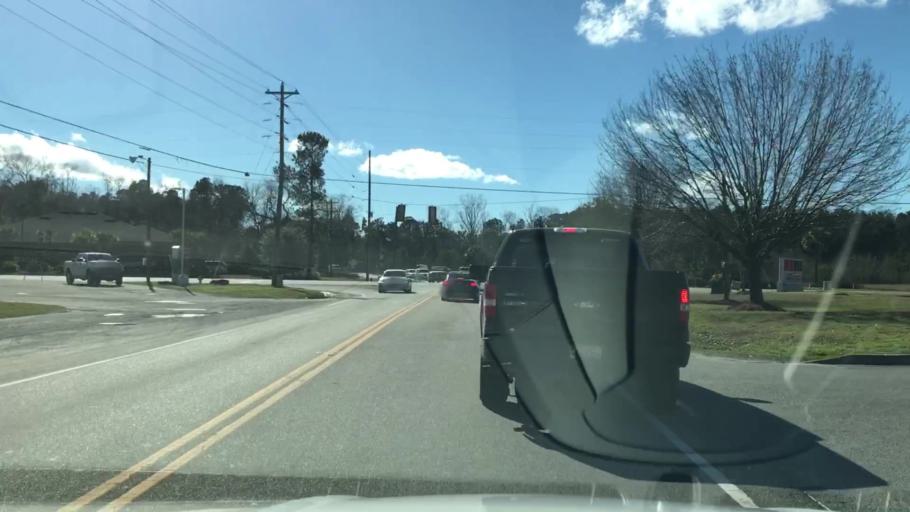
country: US
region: South Carolina
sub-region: Dorchester County
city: Summerville
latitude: 33.0561
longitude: -80.2377
